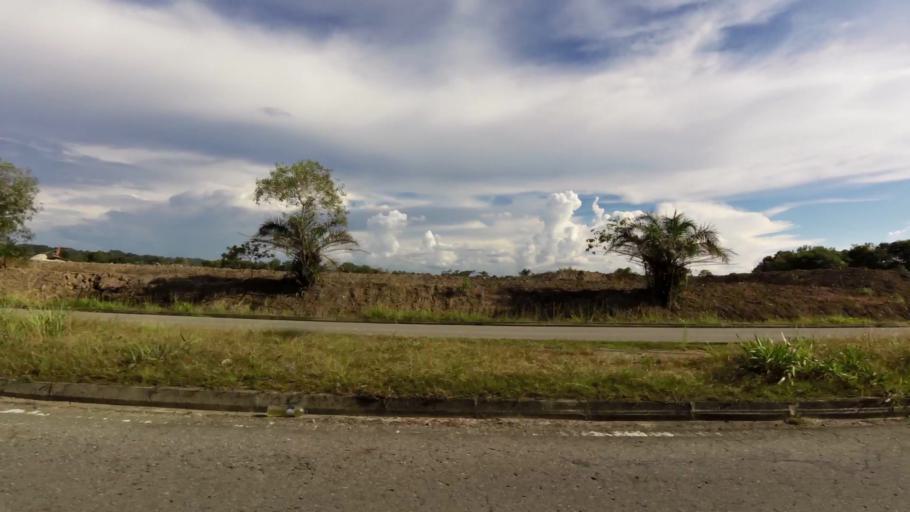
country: BN
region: Brunei and Muara
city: Bandar Seri Begawan
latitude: 4.9720
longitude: 114.9692
